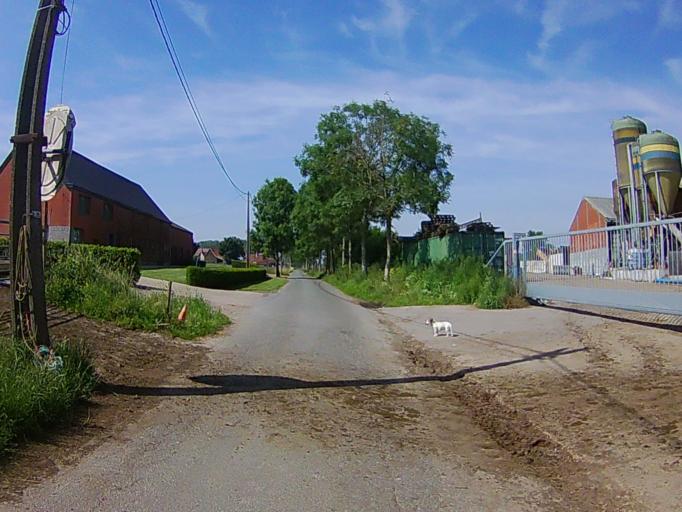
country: BE
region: Flanders
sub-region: Provincie Oost-Vlaanderen
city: Kruibeke
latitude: 51.1698
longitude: 4.2756
